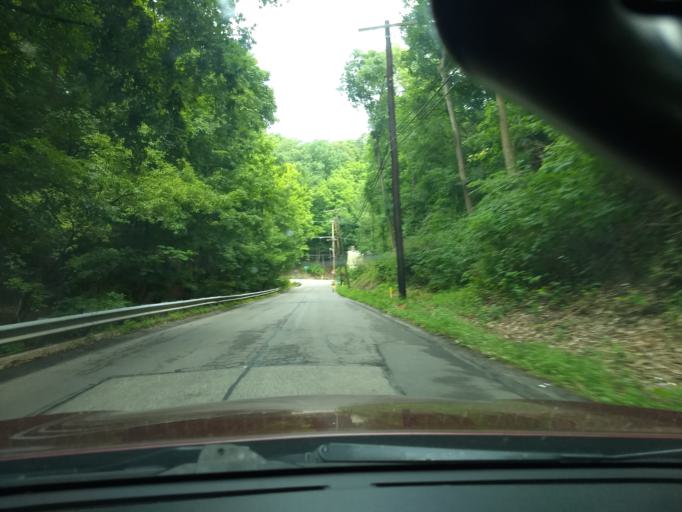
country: US
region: Pennsylvania
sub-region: Allegheny County
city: Bellevue
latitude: 40.4988
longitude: -80.0477
